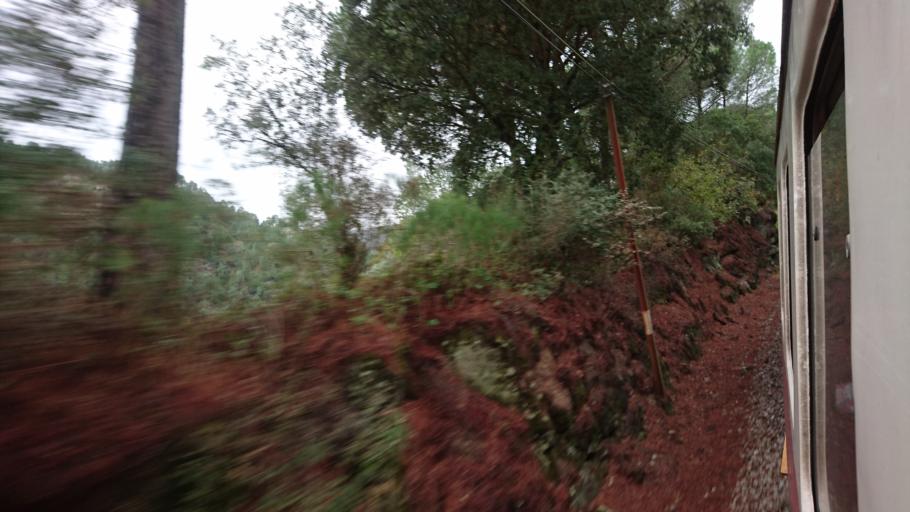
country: PT
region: Viseu
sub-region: Cinfaes
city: Cinfaes
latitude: 41.0914
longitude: -8.0594
